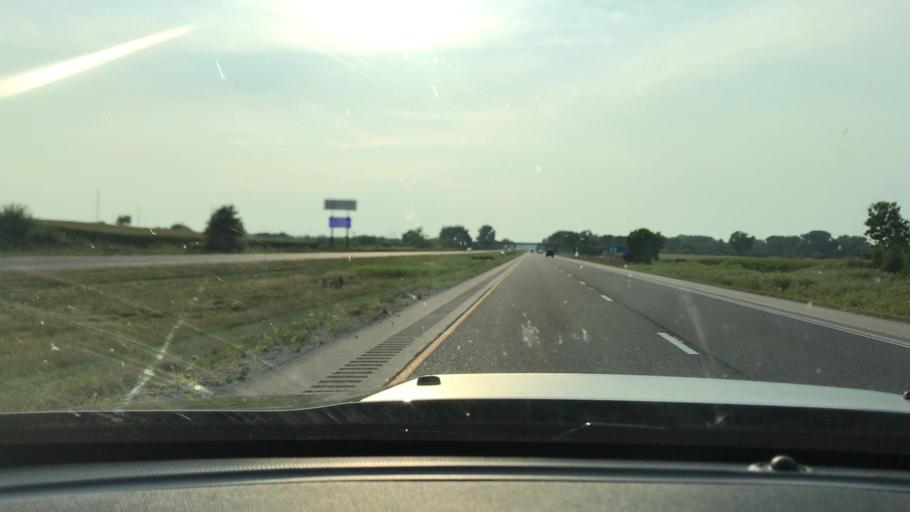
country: US
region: Illinois
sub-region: Henry County
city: Kewanee
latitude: 41.3965
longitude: -89.8694
